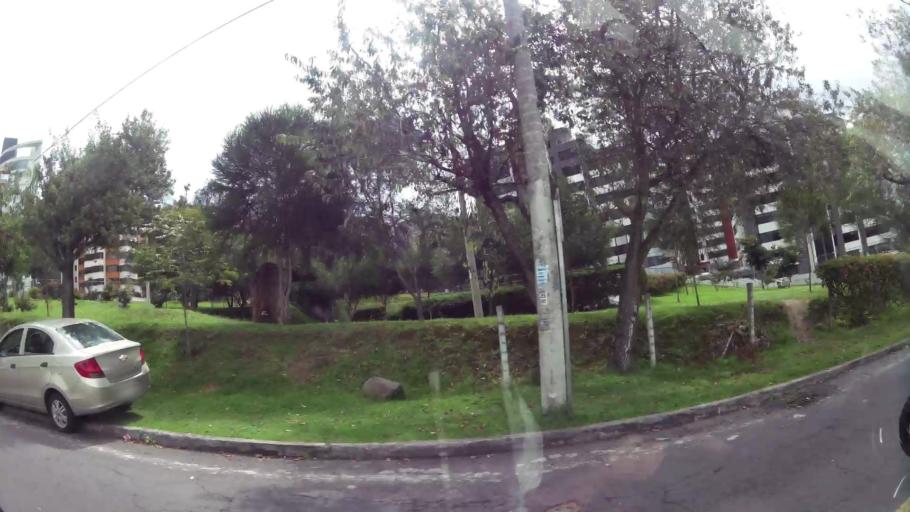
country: EC
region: Pichincha
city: Quito
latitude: -0.1628
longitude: -78.4947
